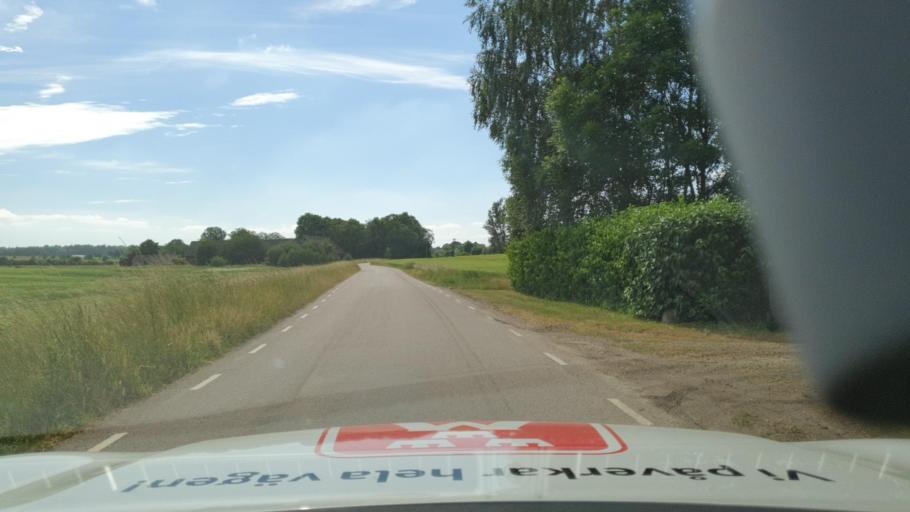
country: SE
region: Skane
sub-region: Sjobo Kommun
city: Sjoebo
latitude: 55.6383
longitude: 13.7871
